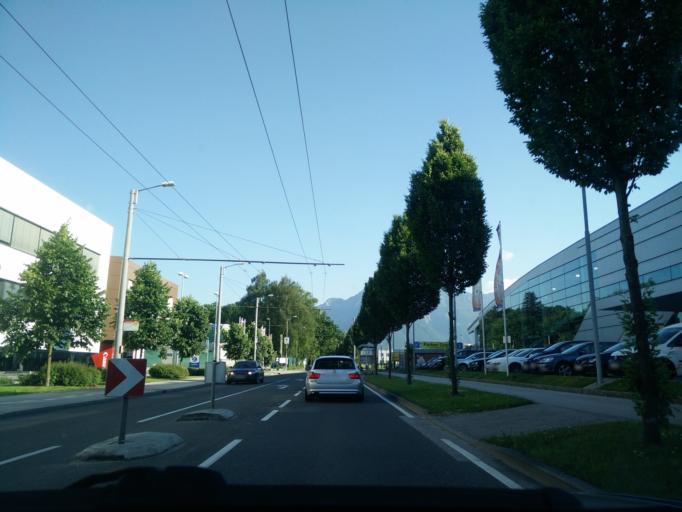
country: AT
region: Salzburg
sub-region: Salzburg Stadt
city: Salzburg
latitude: 47.7976
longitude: 13.0082
